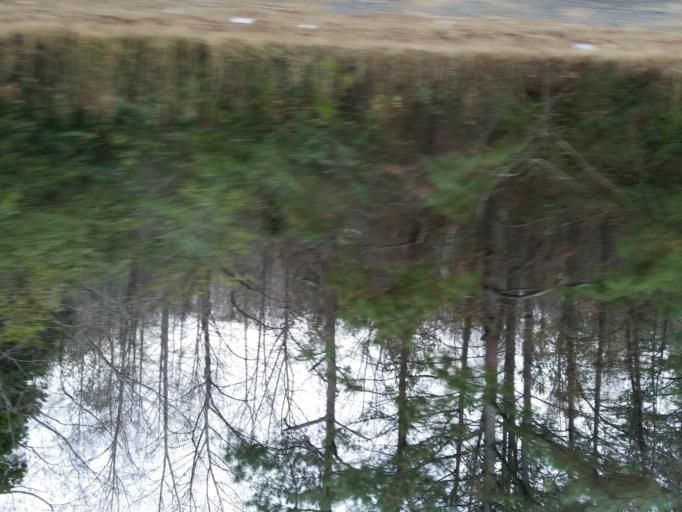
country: US
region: Georgia
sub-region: Dawson County
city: Dawsonville
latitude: 34.3995
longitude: -84.0124
